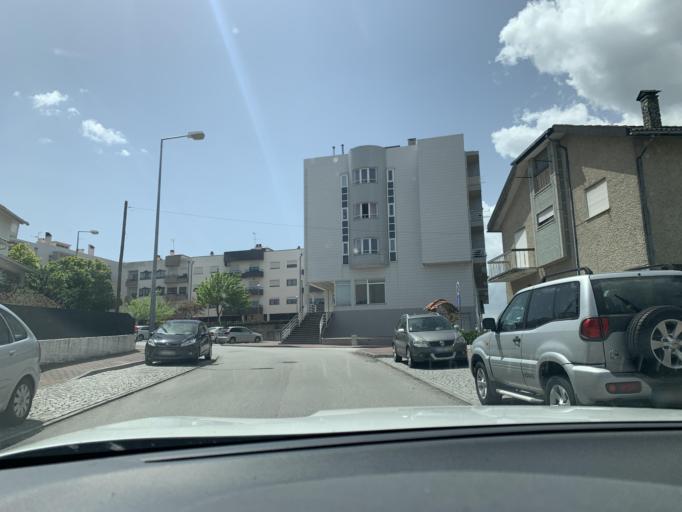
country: PT
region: Viseu
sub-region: Mangualde
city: Mangualde
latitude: 40.6057
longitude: -7.7687
